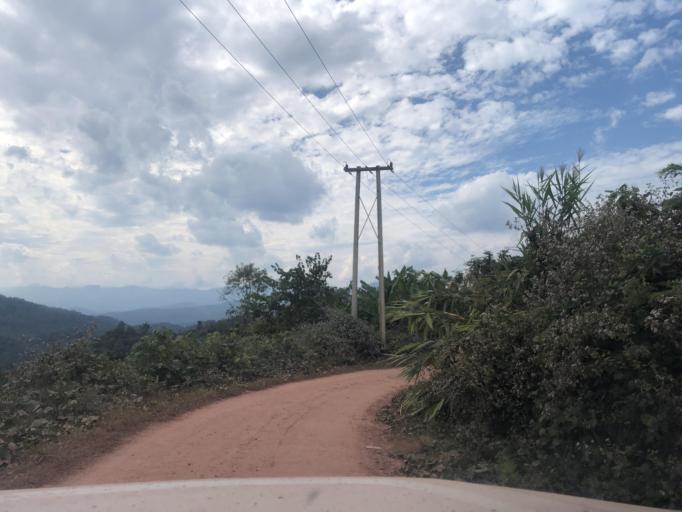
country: CN
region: Yunnan
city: Menglie
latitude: 22.1201
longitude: 101.7378
